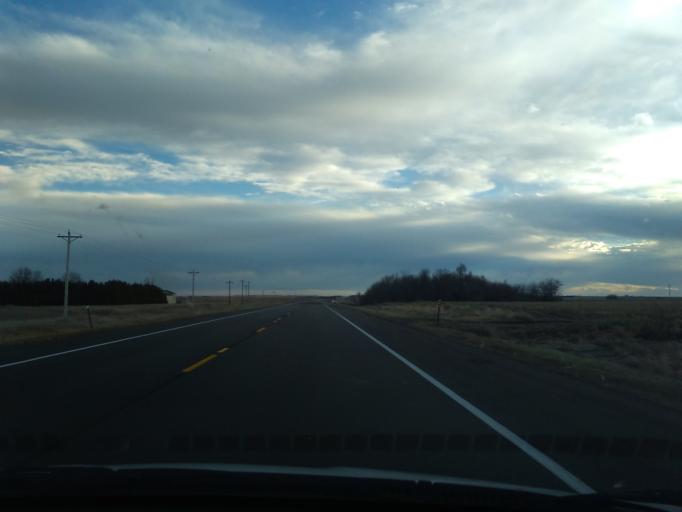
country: US
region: Nebraska
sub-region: Phelps County
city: Holdrege
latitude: 40.3686
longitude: -99.3694
